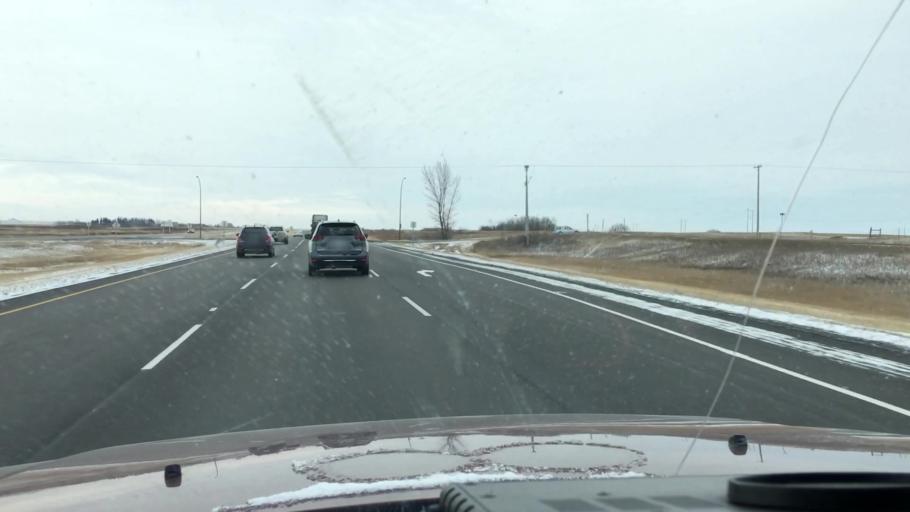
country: CA
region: Saskatchewan
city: Saskatoon
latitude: 51.8544
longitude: -106.5091
